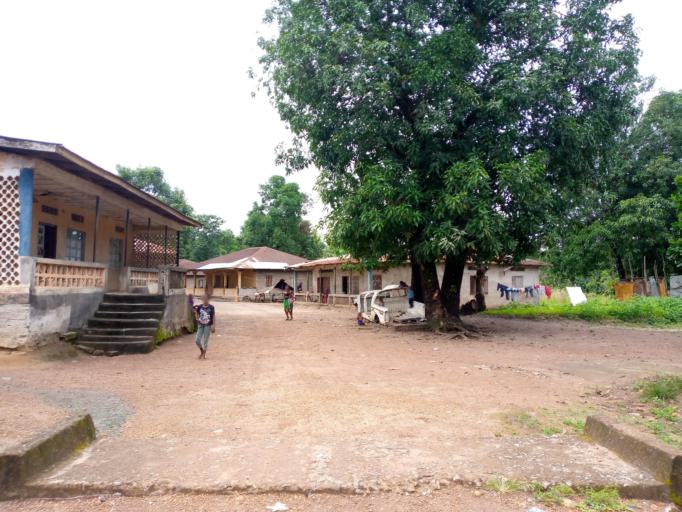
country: SL
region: Northern Province
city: Magburaka
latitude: 8.7186
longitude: -11.9399
